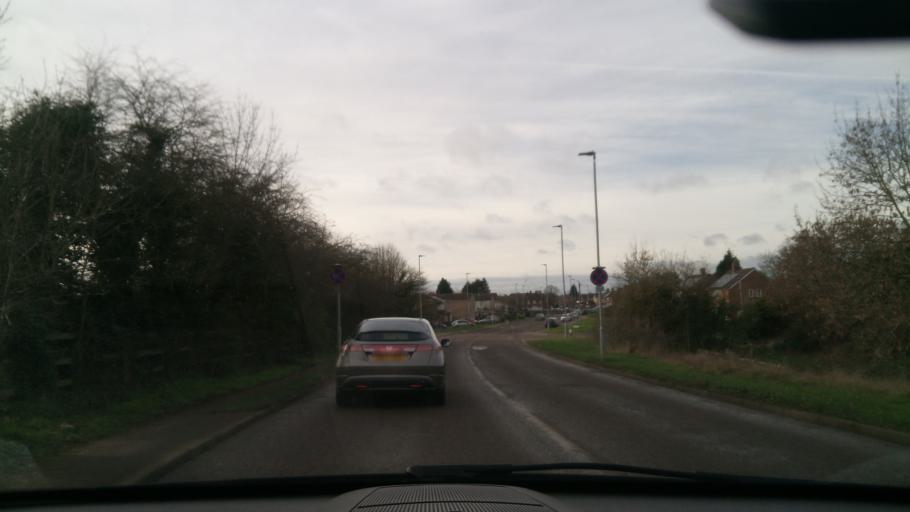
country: GB
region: England
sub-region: Peterborough
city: Peterborough
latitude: 52.6025
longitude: -0.2274
